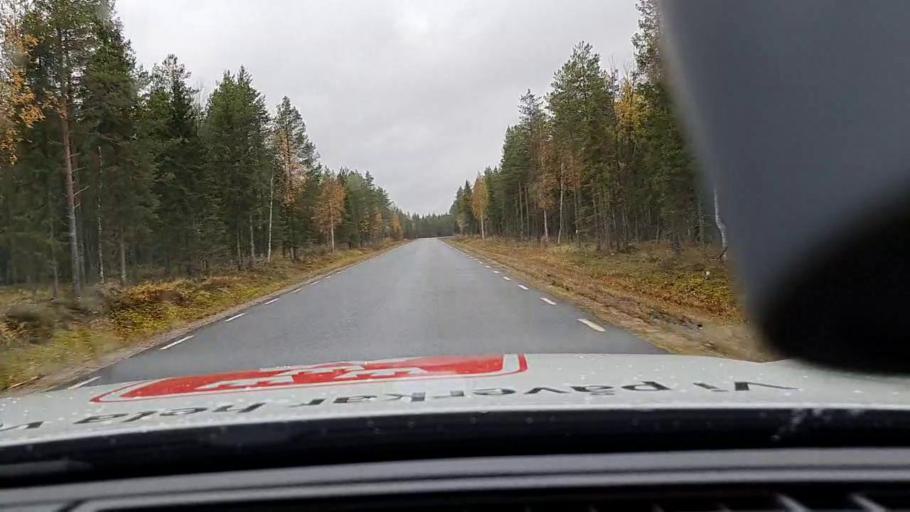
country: SE
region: Norrbotten
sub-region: Haparanda Kommun
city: Haparanda
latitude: 65.9370
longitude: 23.8082
